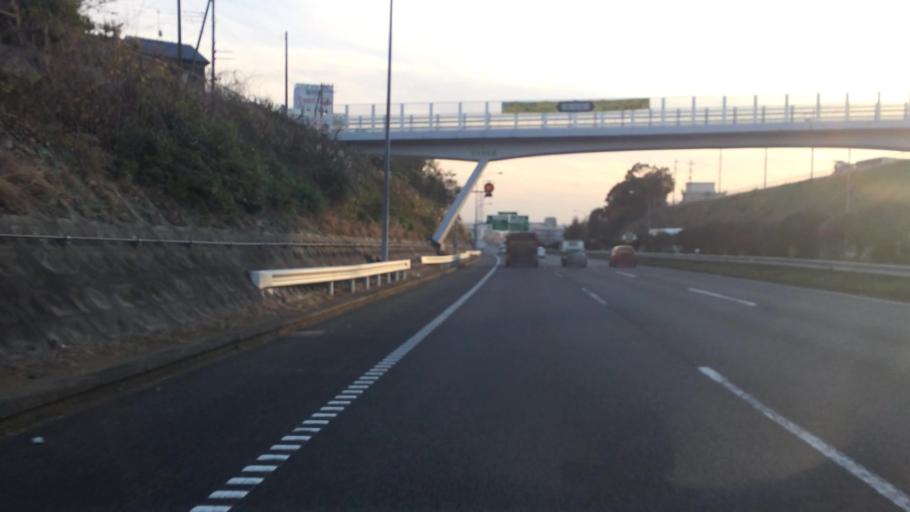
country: JP
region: Kanagawa
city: Yokohama
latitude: 35.5266
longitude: 139.5959
